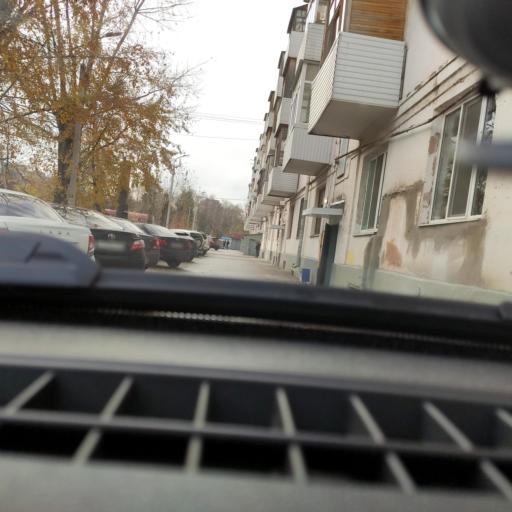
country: RU
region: Bashkortostan
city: Ufa
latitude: 54.7873
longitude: 56.1268
